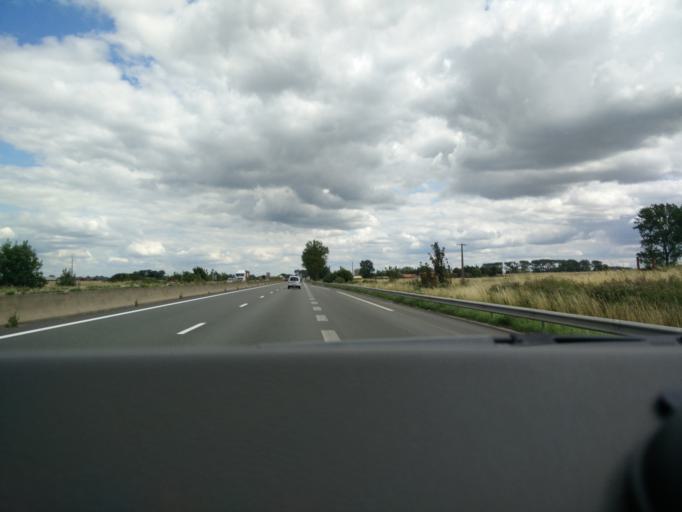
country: FR
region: Nord-Pas-de-Calais
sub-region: Departement du Nord
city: Socx
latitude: 50.9469
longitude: 2.4373
